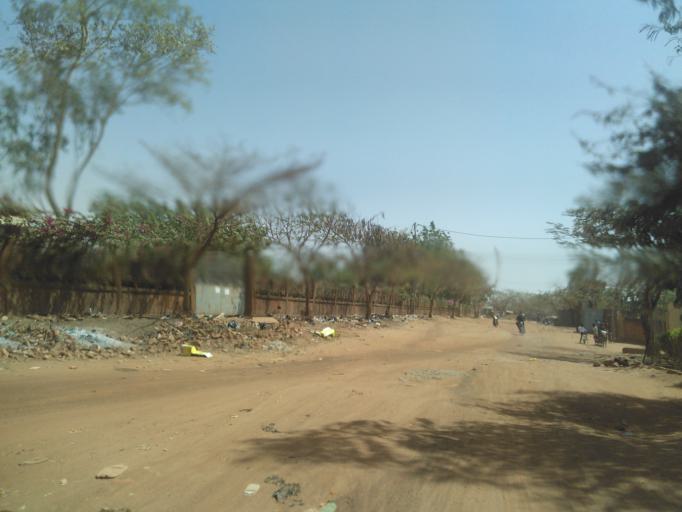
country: BF
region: Centre
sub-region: Kadiogo Province
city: Ouagadougou
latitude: 12.3924
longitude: -1.5694
